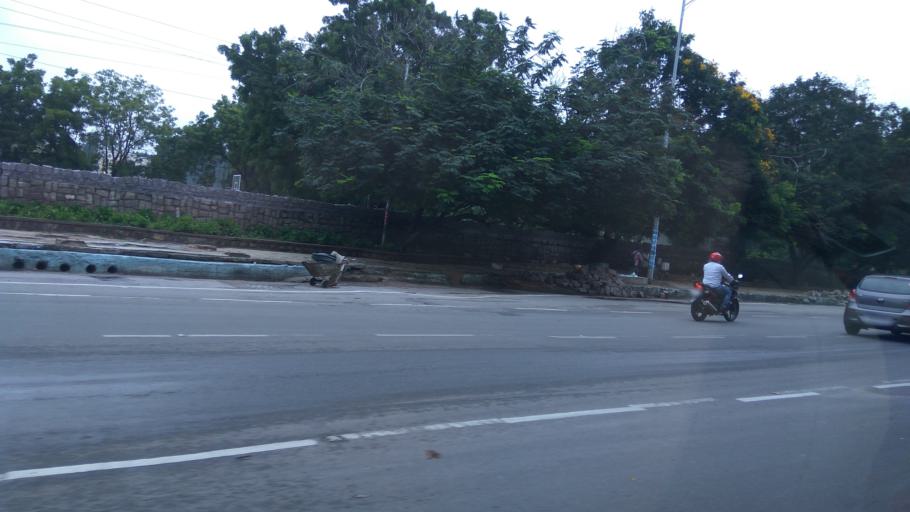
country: IN
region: Telangana
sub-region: Rangareddi
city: Quthbullapur
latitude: 17.4428
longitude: 78.4592
